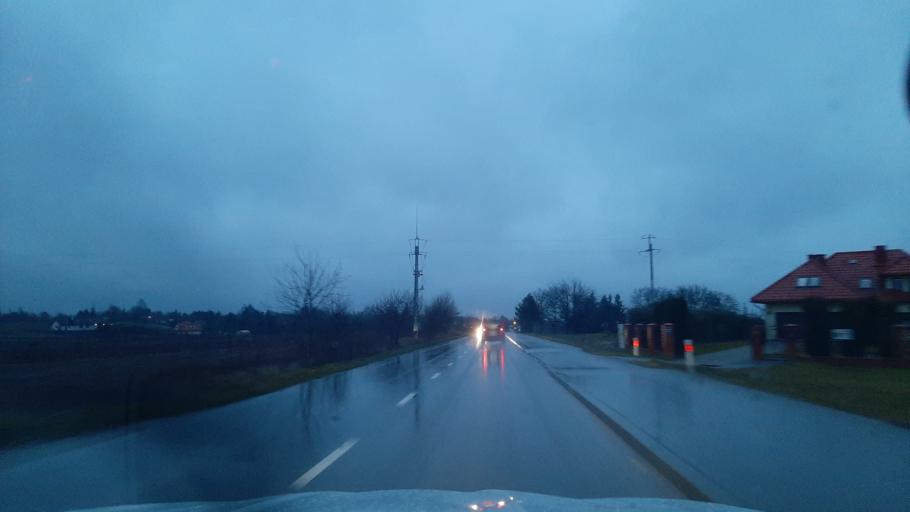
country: PL
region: Lublin Voivodeship
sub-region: Powiat lubelski
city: Jastkow
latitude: 51.3267
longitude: 22.5208
